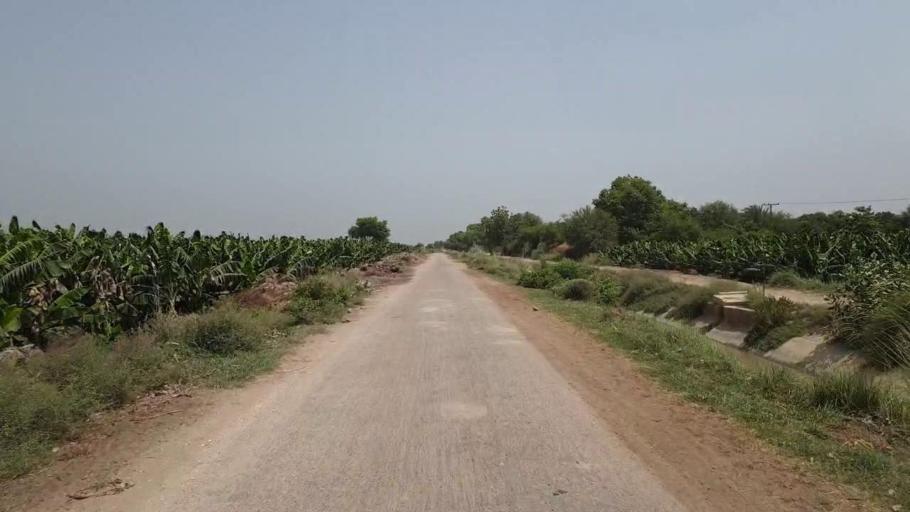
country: PK
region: Sindh
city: Nawabshah
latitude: 26.2855
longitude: 68.3103
